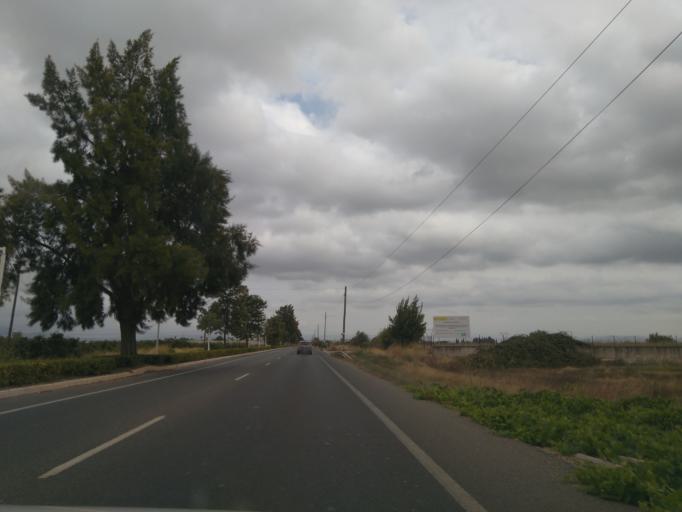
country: ES
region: Valencia
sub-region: Provincia de Valencia
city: Carlet
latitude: 39.2149
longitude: -0.5146
